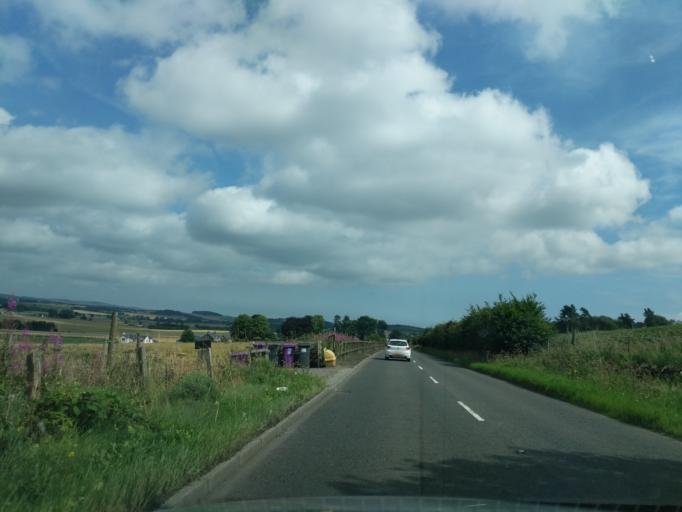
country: GB
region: Scotland
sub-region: Angus
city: Muirhead
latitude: 56.5000
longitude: -3.0953
